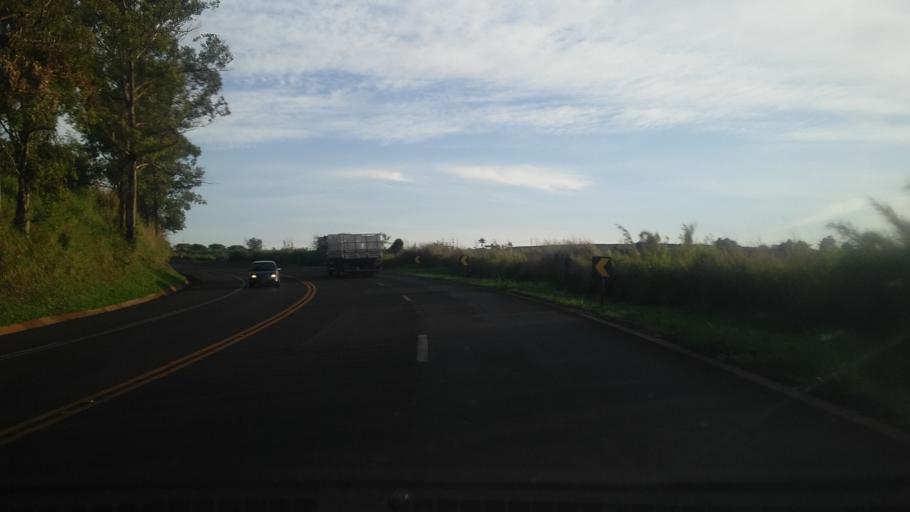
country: BR
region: Parana
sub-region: Bandeirantes
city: Bandeirantes
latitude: -23.1794
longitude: -50.6235
